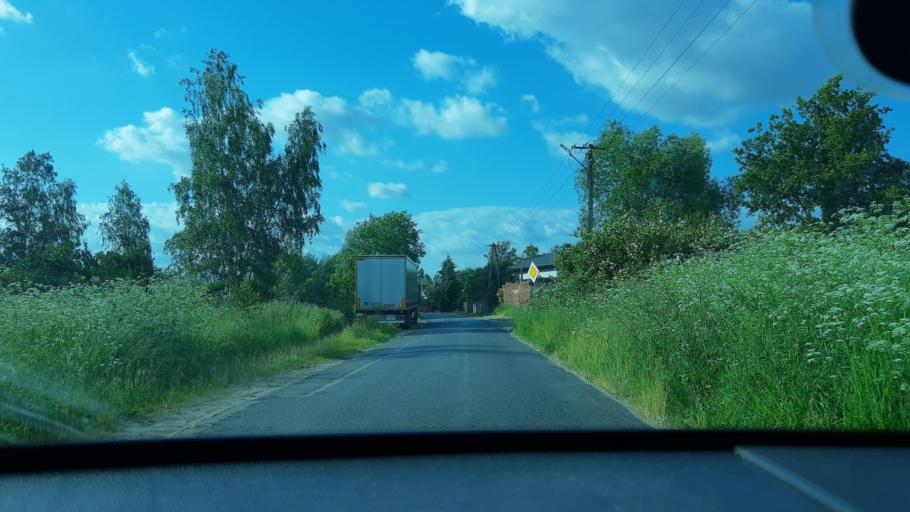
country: PL
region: Lodz Voivodeship
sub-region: Powiat zdunskowolski
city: Zapolice
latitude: 51.5236
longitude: 18.8432
